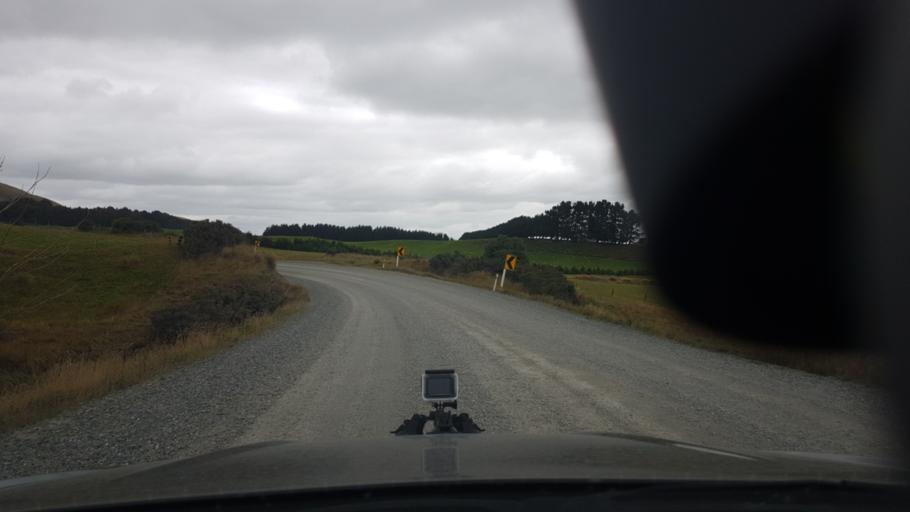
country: NZ
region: Otago
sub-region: Clutha District
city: Papatowai
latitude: -46.3188
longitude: 169.3694
